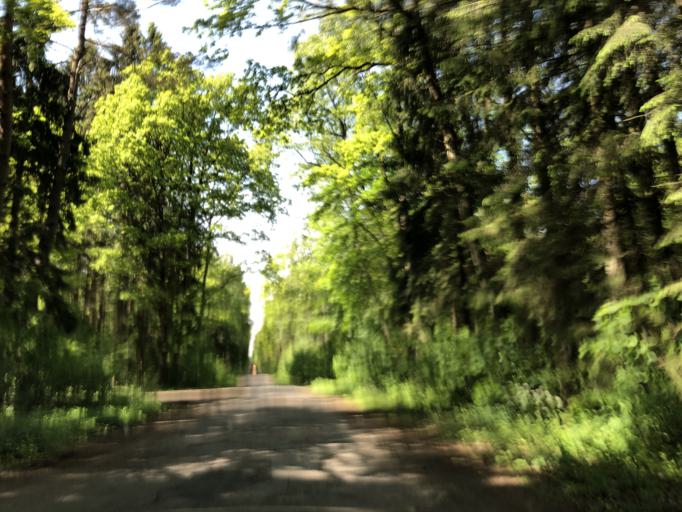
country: PL
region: West Pomeranian Voivodeship
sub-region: Powiat kolobrzeski
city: Dygowo
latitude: 54.0767
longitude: 15.7434
